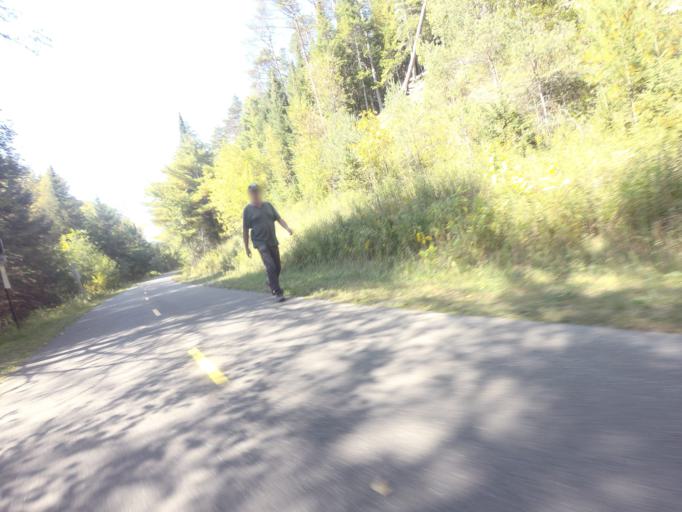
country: CA
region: Quebec
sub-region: Laurentides
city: Mont-Tremblant
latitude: 46.1287
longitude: -74.5868
